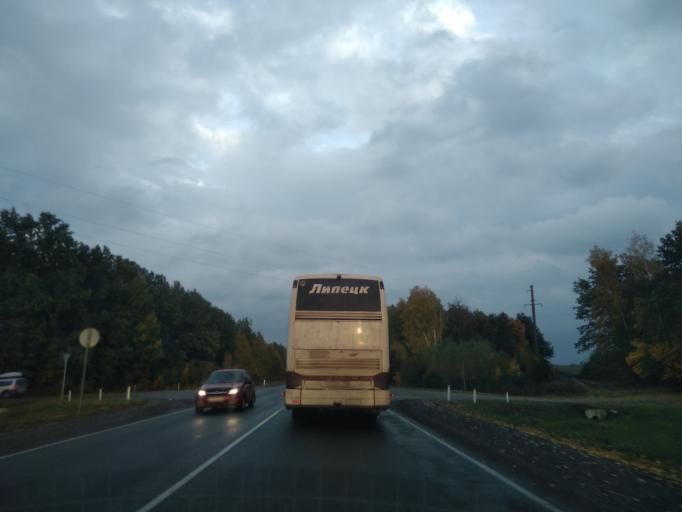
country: RU
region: Lipetsk
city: Borinskoye
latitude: 52.5991
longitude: 39.3143
